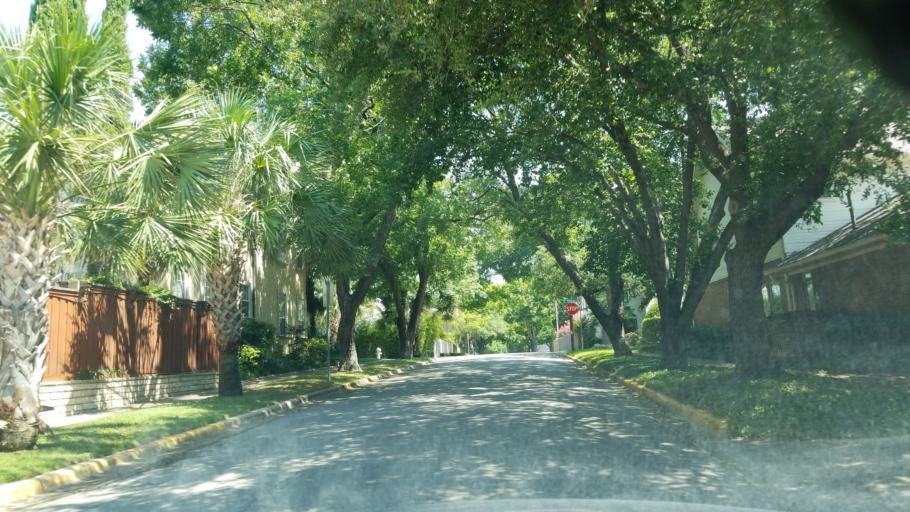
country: US
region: Texas
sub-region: Dallas County
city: Highland Park
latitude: 32.8484
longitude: -96.7809
